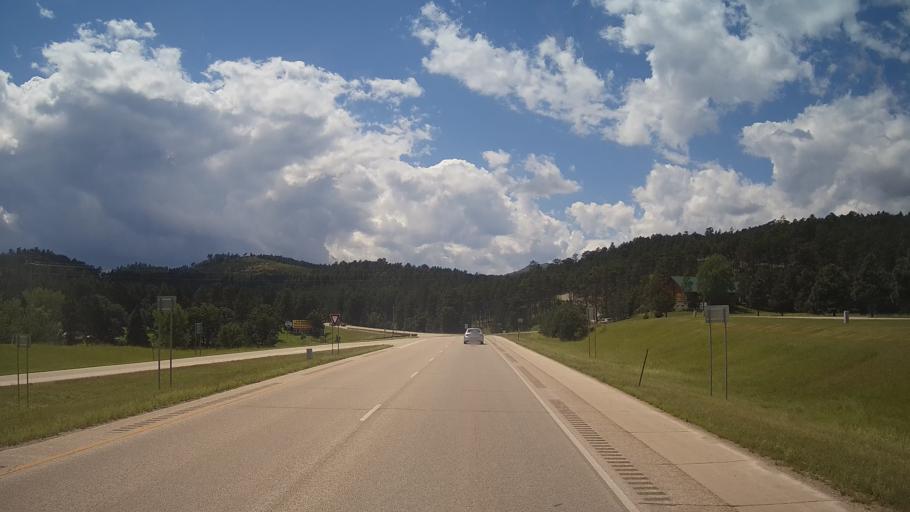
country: US
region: South Dakota
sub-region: Pennington County
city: Colonial Pine Hills
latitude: 43.9594
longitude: -103.3595
